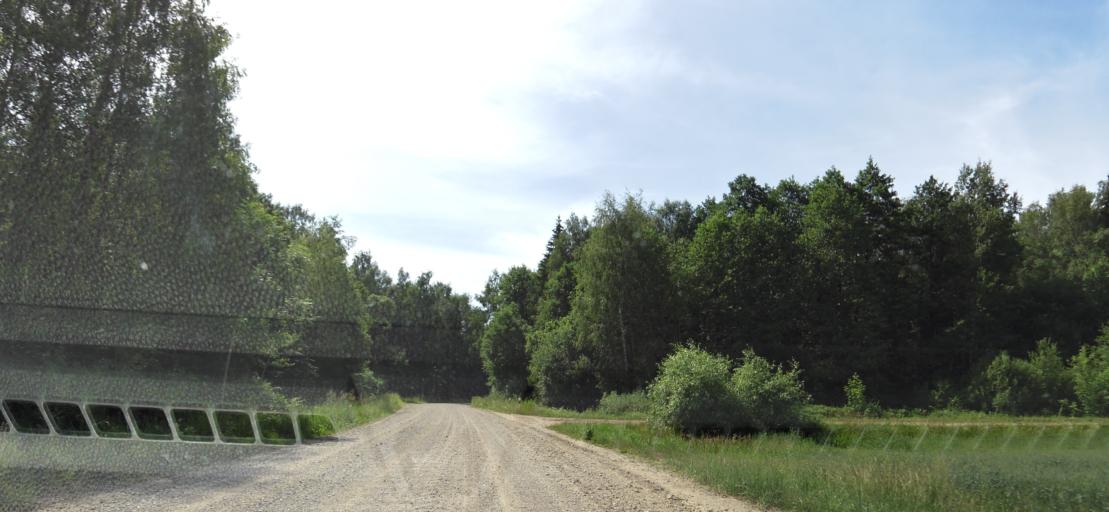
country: LT
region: Panevezys
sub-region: Panevezys City
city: Panevezys
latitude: 55.8821
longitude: 24.3122
